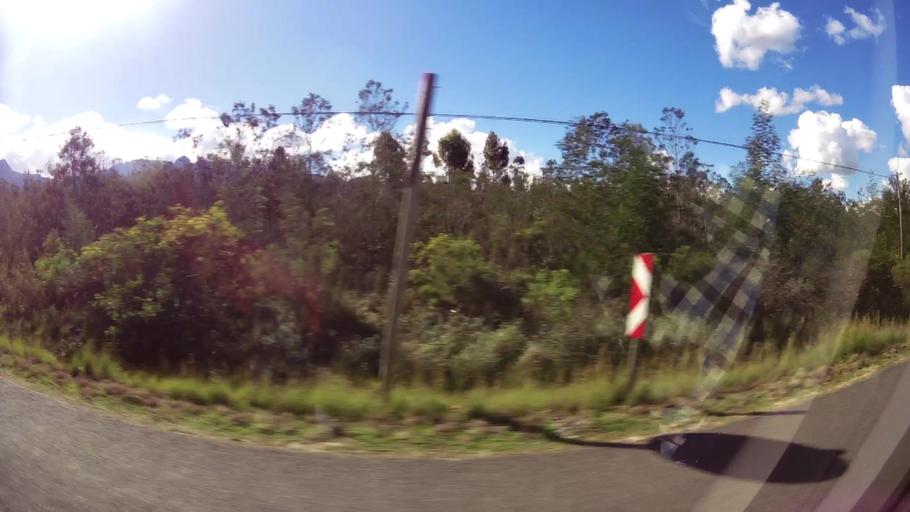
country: ZA
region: Western Cape
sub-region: Overberg District Municipality
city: Swellendam
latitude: -34.0359
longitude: 20.4237
